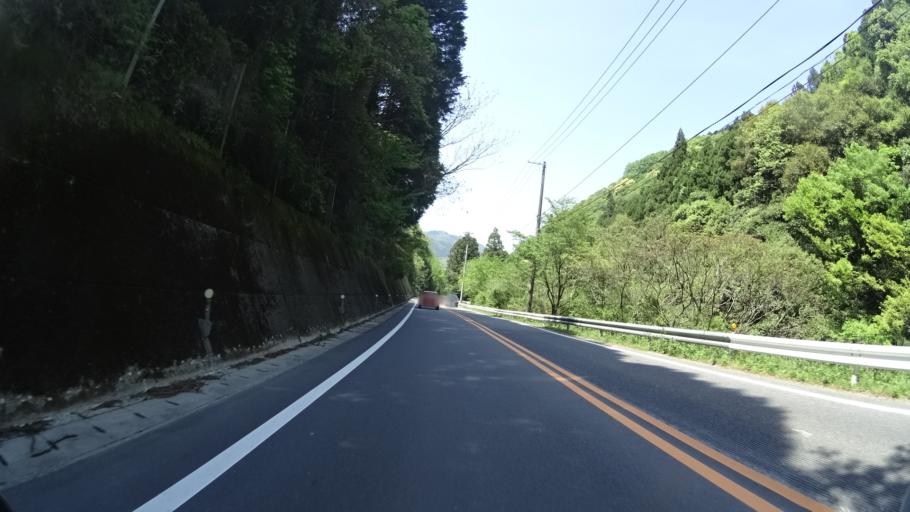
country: JP
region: Ehime
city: Hojo
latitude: 33.9611
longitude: 132.9082
